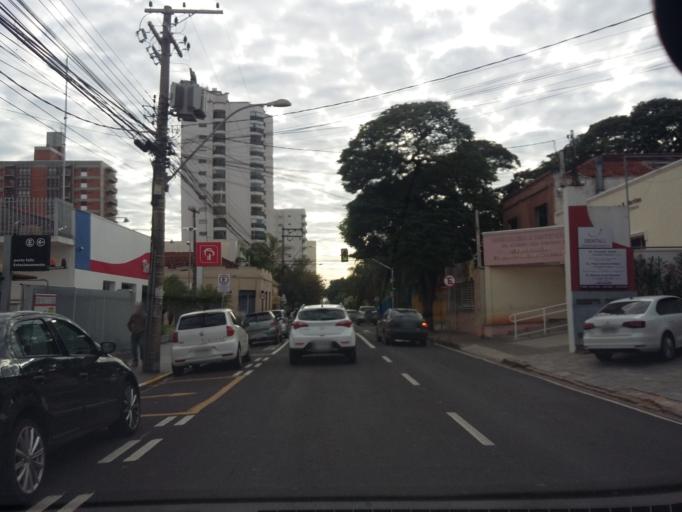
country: BR
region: Sao Paulo
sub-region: Sao Jose Do Rio Preto
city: Sao Jose do Rio Preto
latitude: -20.8181
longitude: -49.3879
